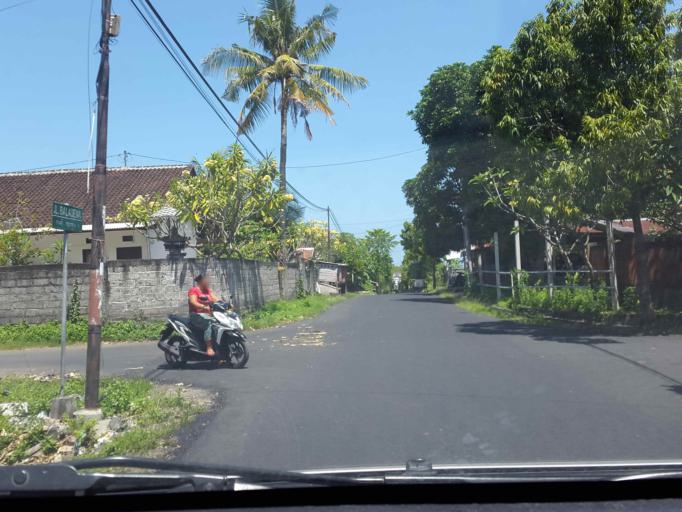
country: ID
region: Bali
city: Semarapura
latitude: -8.5394
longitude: 115.4057
